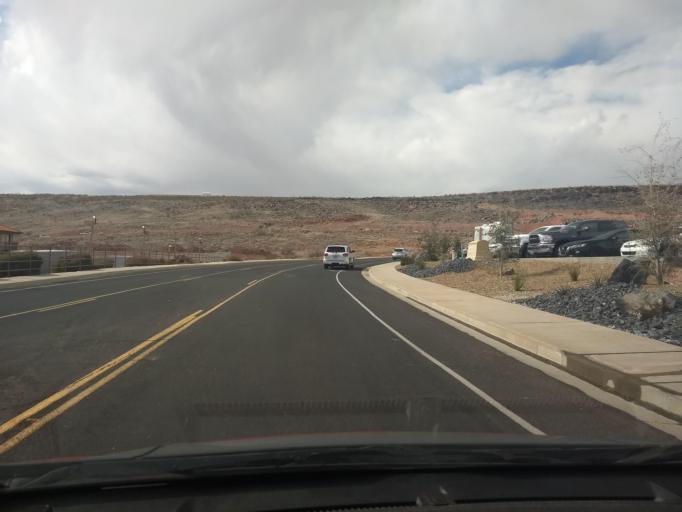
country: US
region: Utah
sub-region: Washington County
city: Saint George
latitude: 37.0850
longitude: -113.5850
